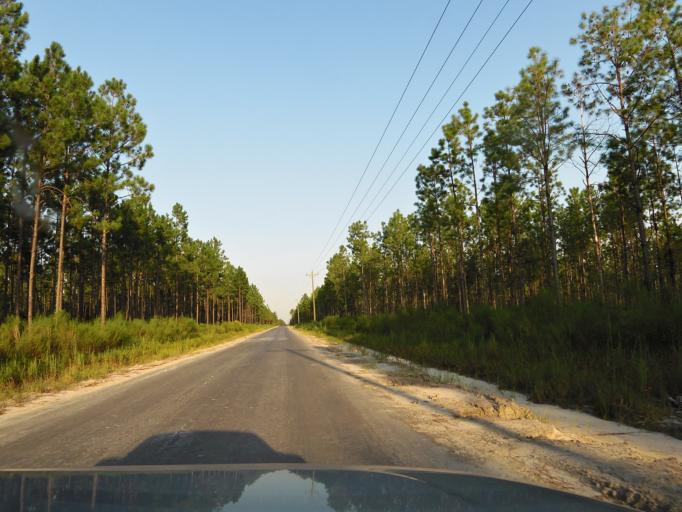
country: US
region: Florida
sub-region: Baker County
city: Macclenny
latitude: 30.3951
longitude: -82.1187
